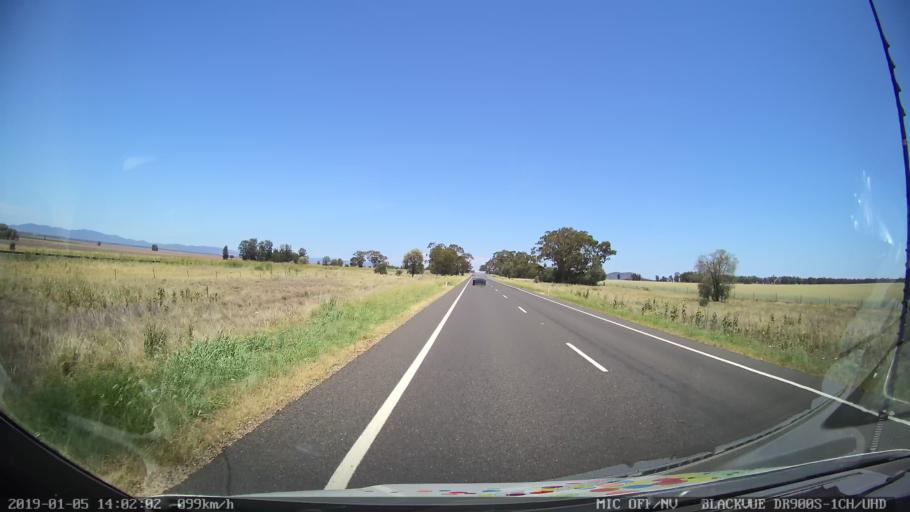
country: AU
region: New South Wales
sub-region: Gunnedah
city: Gunnedah
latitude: -31.1757
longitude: 150.3326
